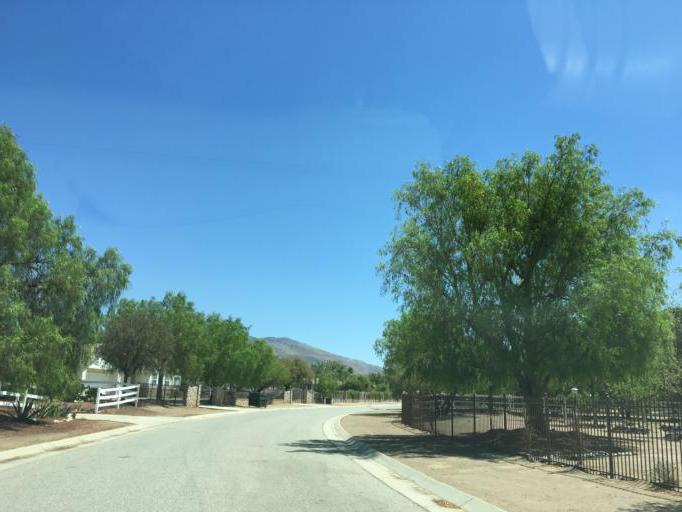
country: US
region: California
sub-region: Los Angeles County
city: Agua Dulce
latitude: 34.5171
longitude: -118.3064
